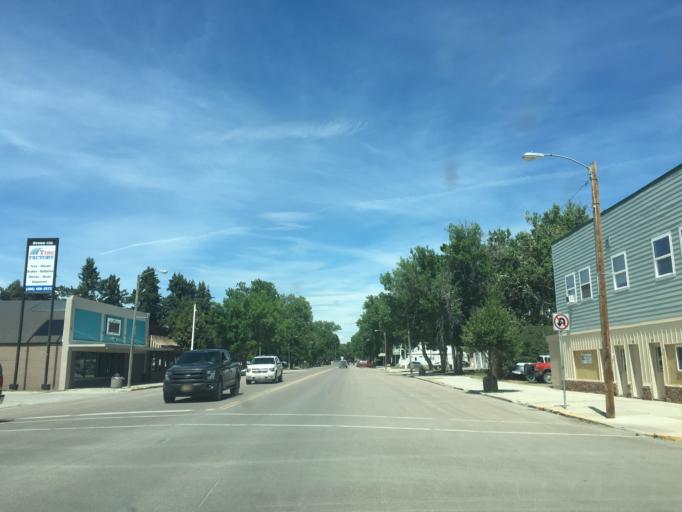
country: US
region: Montana
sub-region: Teton County
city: Choteau
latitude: 47.8139
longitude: -112.1848
